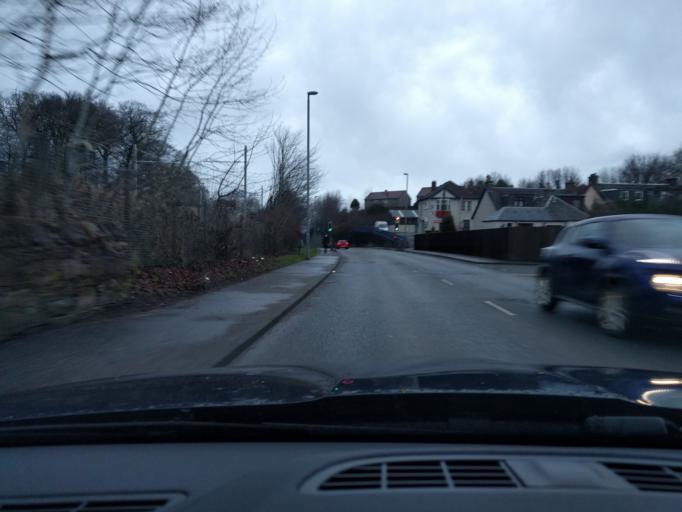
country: GB
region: Scotland
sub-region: Falkirk
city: Falkirk
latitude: 55.9932
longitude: -3.7523
